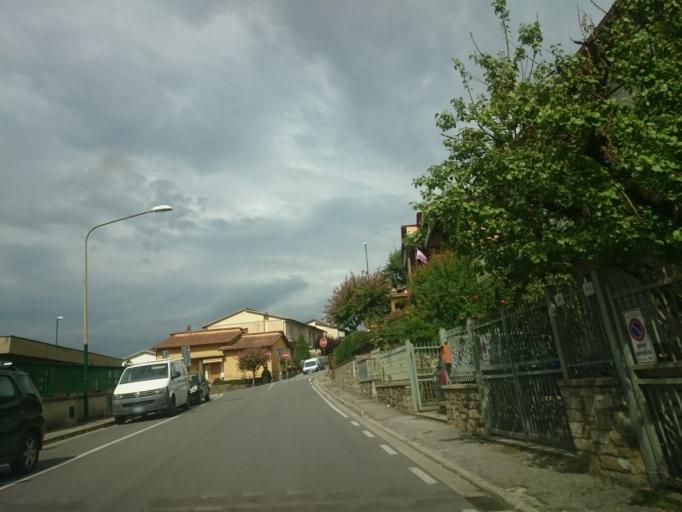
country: IT
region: Tuscany
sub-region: Province of Florence
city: Greve in Chianti
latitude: 43.5860
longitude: 11.3166
